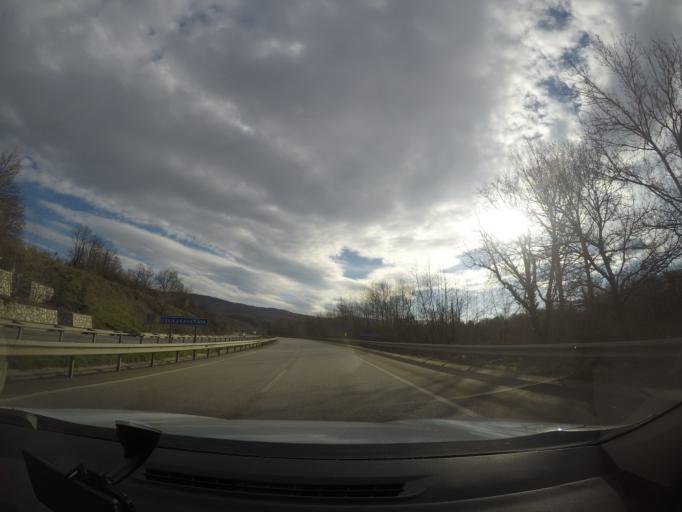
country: TR
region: Bursa
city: Tahtakopru
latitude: 39.9546
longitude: 29.6709
